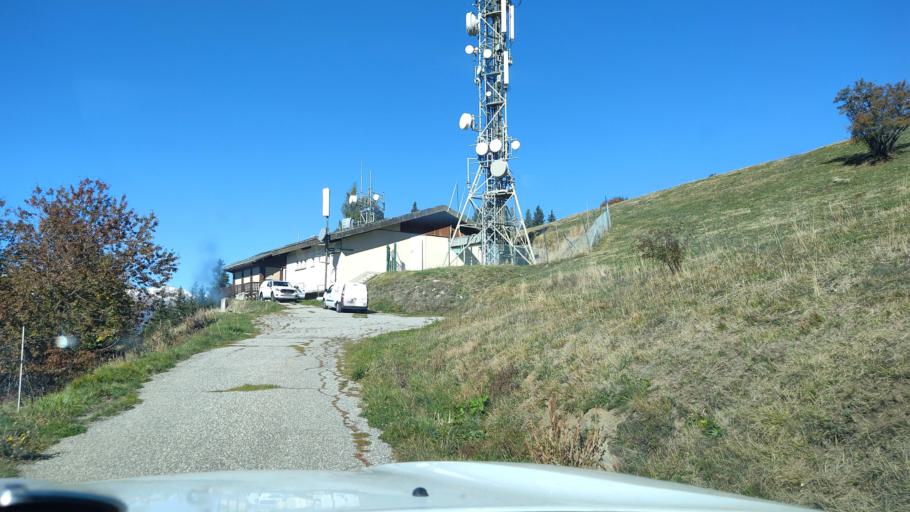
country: FR
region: Rhone-Alpes
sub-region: Departement de la Savoie
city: Seez
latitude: 45.6238
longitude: 6.8480
